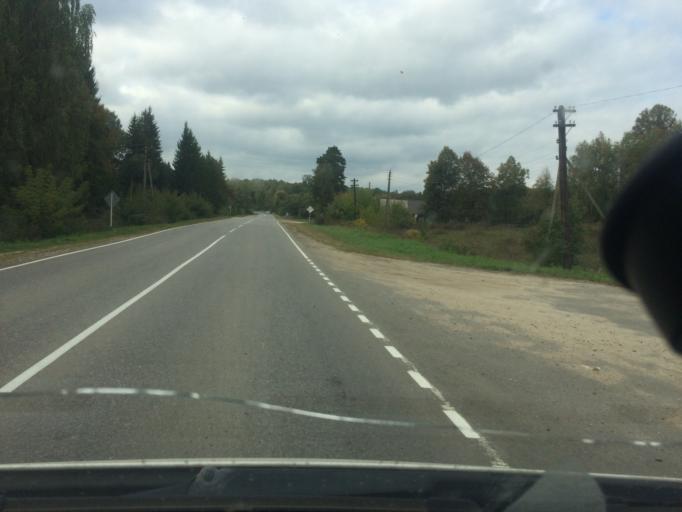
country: RU
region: Tula
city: Suvorov
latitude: 54.0508
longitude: 36.5775
